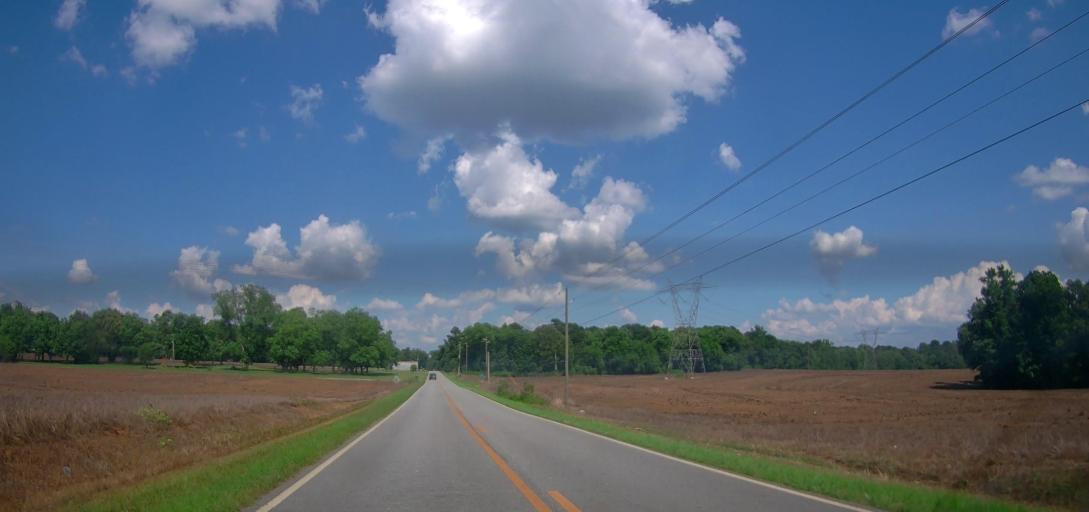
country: US
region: Georgia
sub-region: Henry County
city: Locust Grove
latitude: 33.2194
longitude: -84.0880
